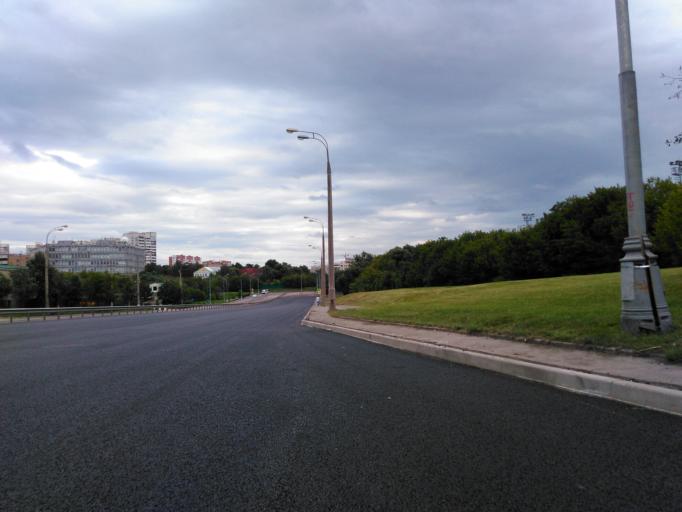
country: RU
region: Moskovskaya
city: Bogorodskoye
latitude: 55.8081
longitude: 37.6981
